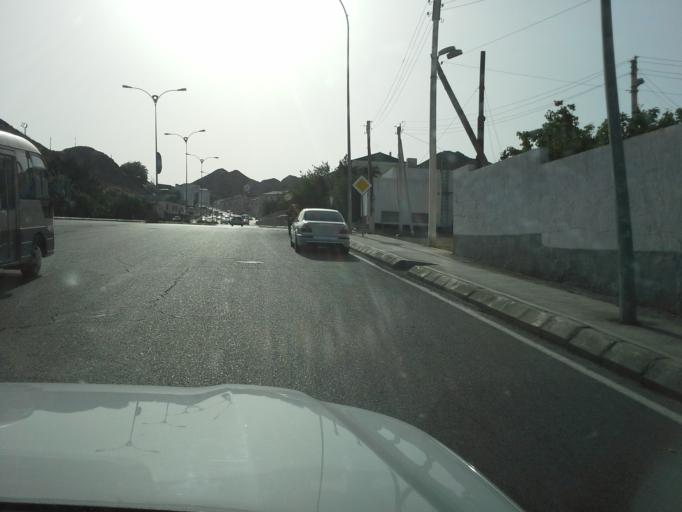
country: TM
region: Balkan
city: Turkmenbasy
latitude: 40.0020
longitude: 52.9859
